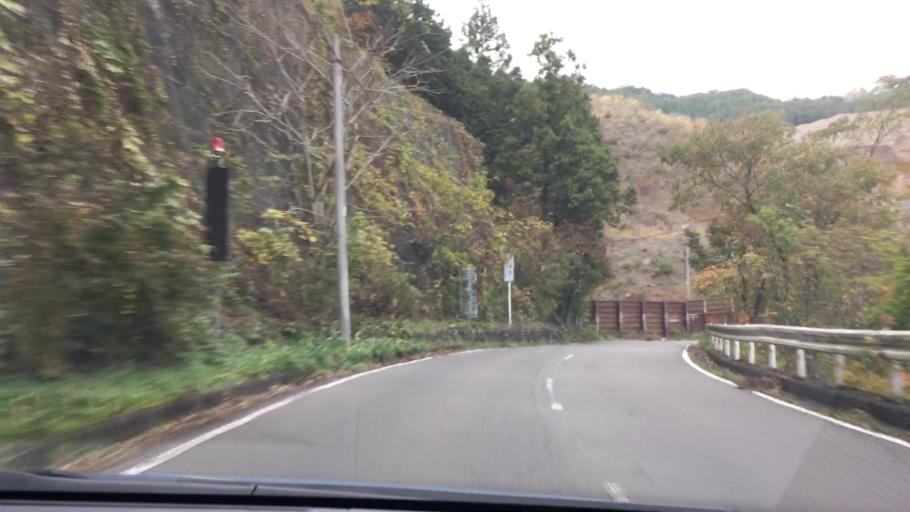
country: JP
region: Yamanashi
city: Uenohara
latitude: 35.5550
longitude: 139.1380
